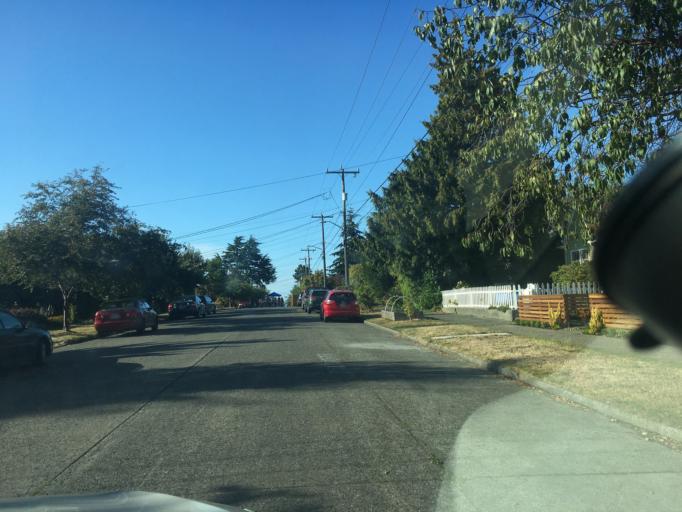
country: US
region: Washington
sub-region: King County
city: Shoreline
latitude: 47.6873
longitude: -122.3930
